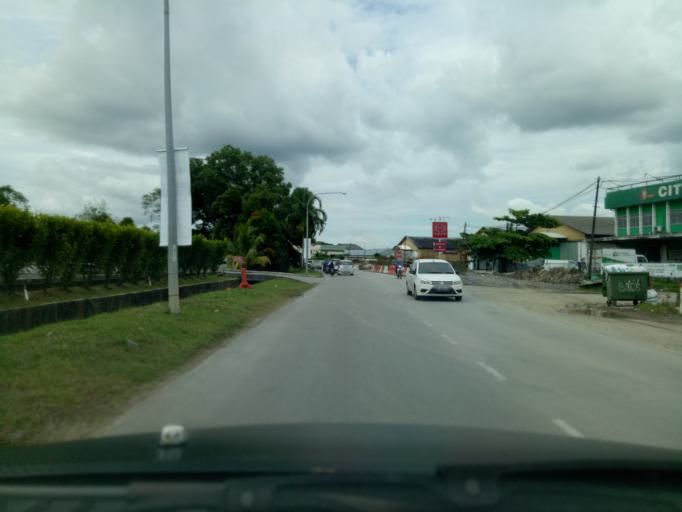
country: MY
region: Sarawak
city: Kuching
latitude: 1.5526
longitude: 110.3767
